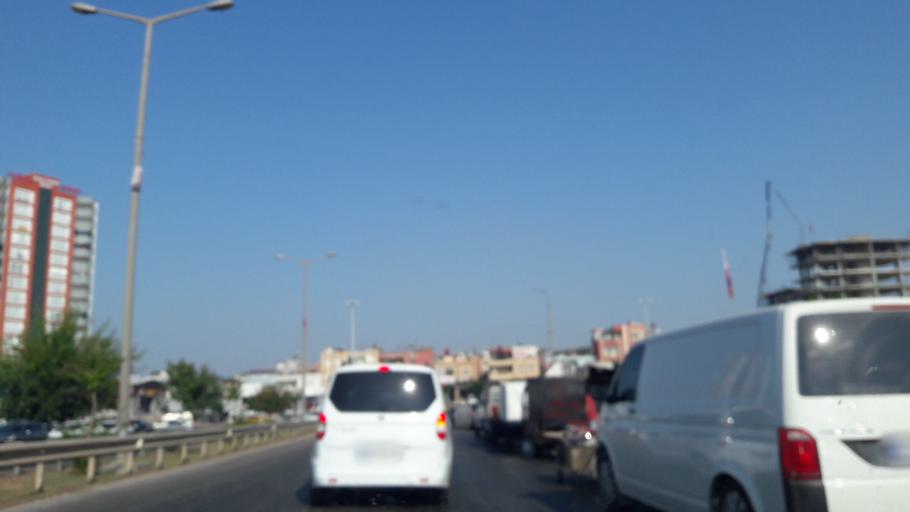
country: TR
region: Adana
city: Yuregir
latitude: 37.0243
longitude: 35.4001
